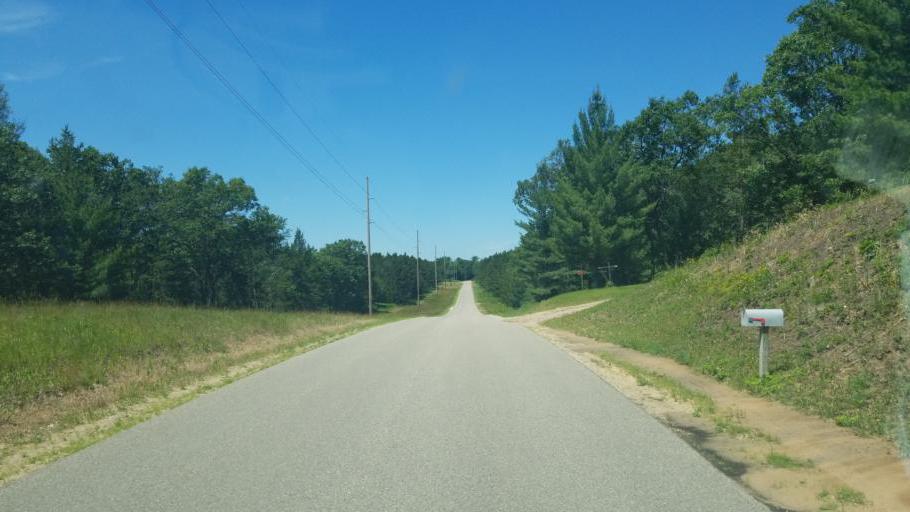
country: US
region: Wisconsin
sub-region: Adams County
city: Friendship
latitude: 43.9816
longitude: -89.9459
